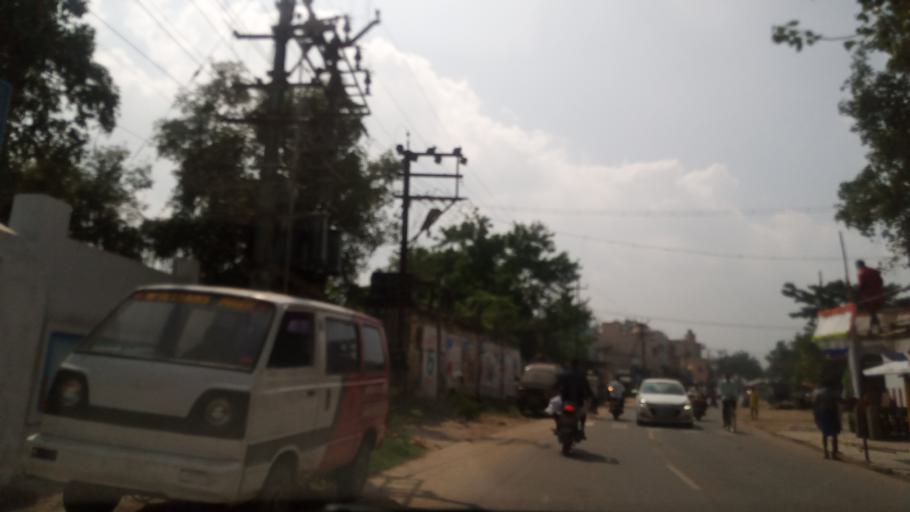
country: IN
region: Tamil Nadu
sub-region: Vellore
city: Arakkonam
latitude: 13.0780
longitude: 79.6717
